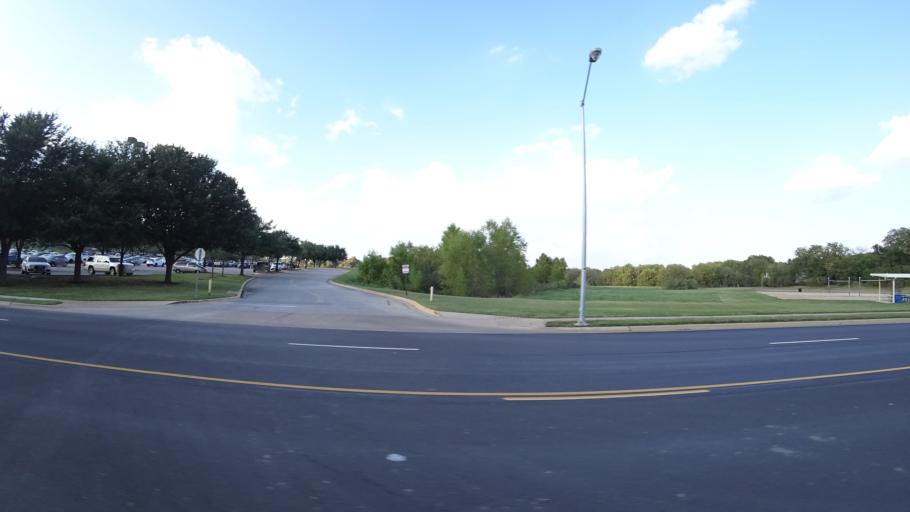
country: US
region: Texas
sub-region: Williamson County
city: Round Rock
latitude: 30.4871
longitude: -97.6681
